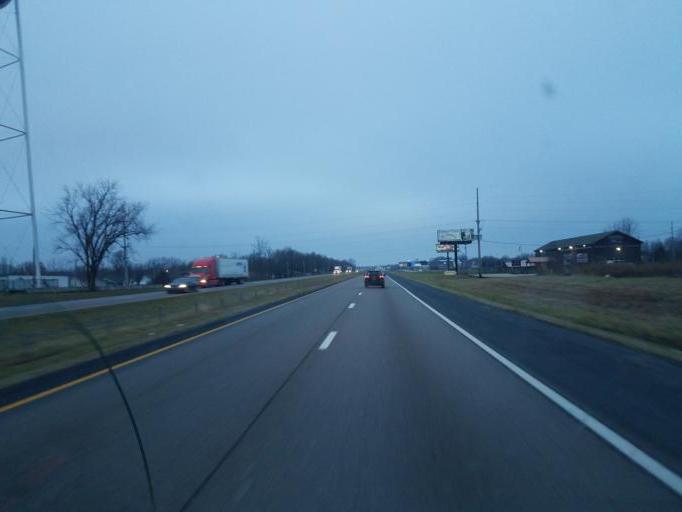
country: US
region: Missouri
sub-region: Phelps County
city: Saint James
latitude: 38.0108
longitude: -91.6024
